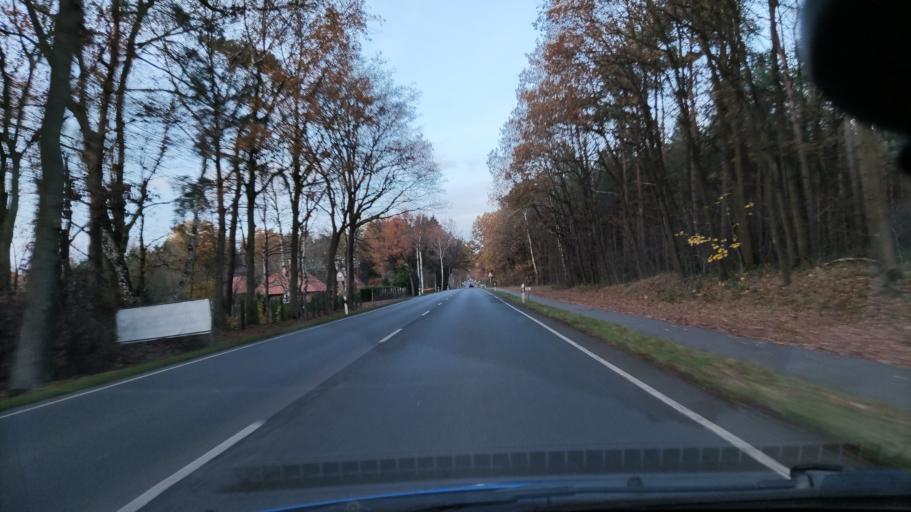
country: DE
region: Lower Saxony
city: Soltau
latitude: 53.0657
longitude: 9.8601
